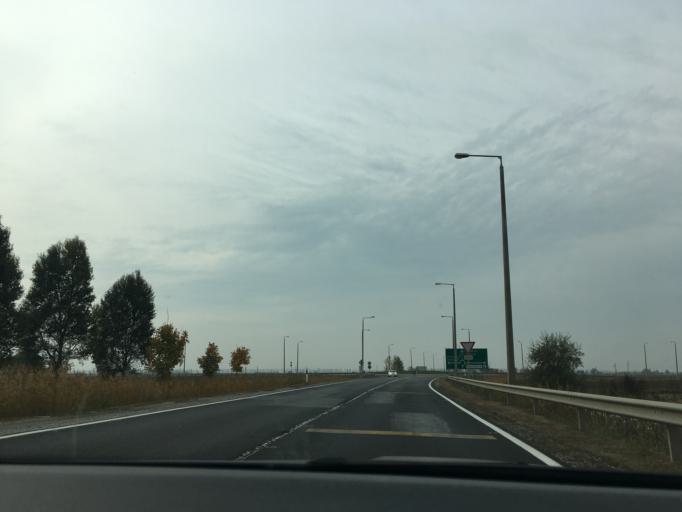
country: HU
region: Hajdu-Bihar
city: Hajduszoboszlo
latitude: 47.4121
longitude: 21.4154
